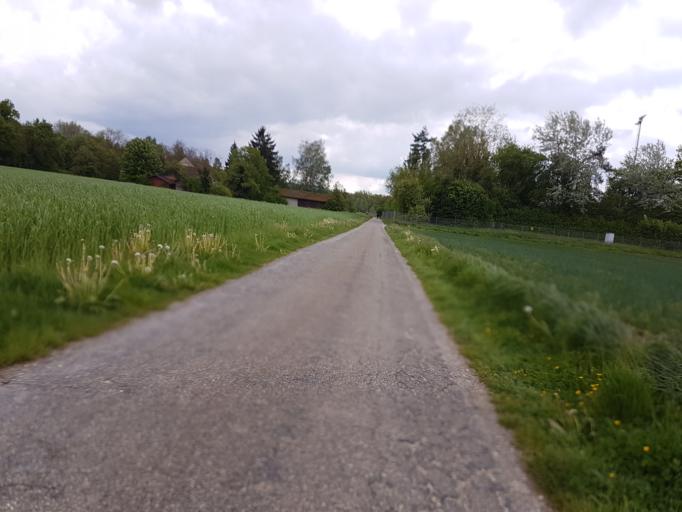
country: CH
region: Aargau
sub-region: Bezirk Brugg
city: Lauffohr (Brugg)
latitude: 47.4929
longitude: 8.2318
